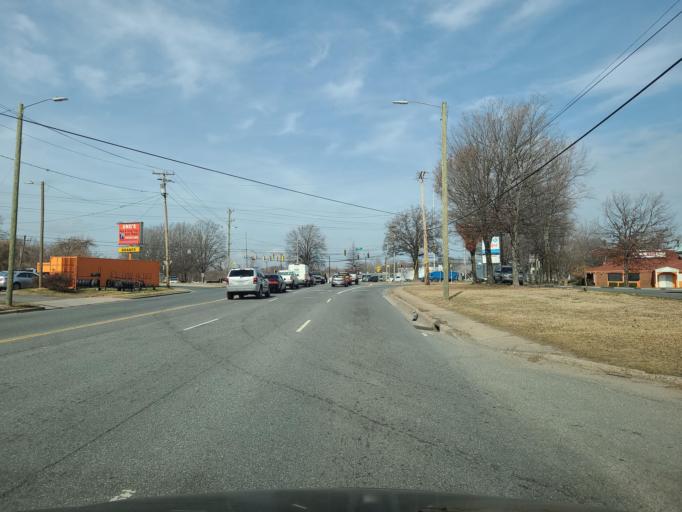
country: US
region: North Carolina
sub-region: Mecklenburg County
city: Charlotte
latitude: 35.2587
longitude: -80.7772
